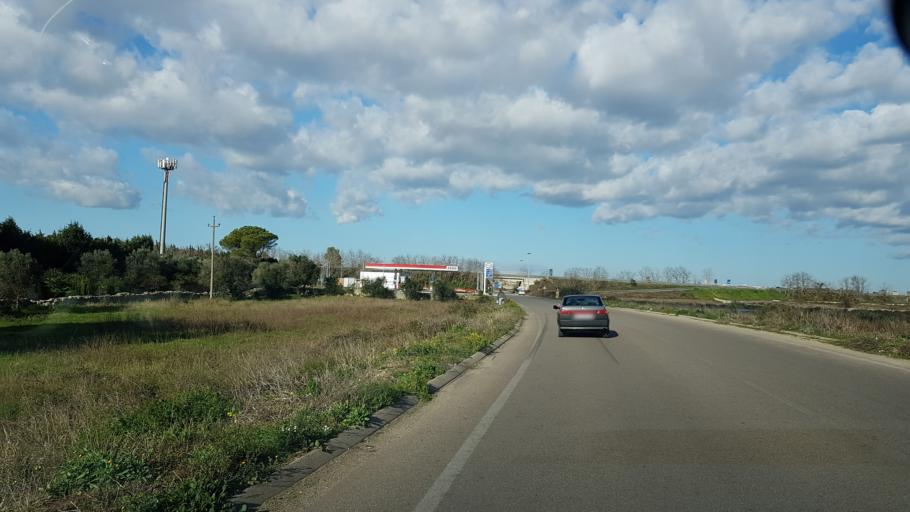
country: IT
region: Apulia
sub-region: Provincia di Lecce
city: Castromediano
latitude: 40.3255
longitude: 18.1885
